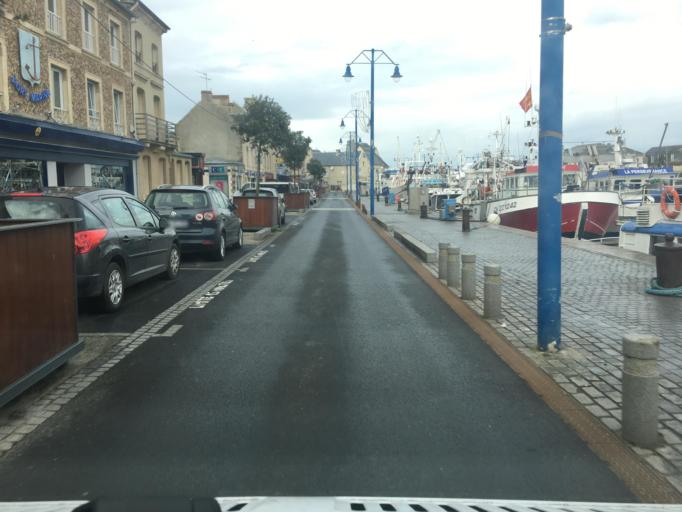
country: FR
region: Lower Normandy
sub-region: Departement du Calvados
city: Port-en-Bessin-Huppain
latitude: 49.3474
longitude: -0.7549
